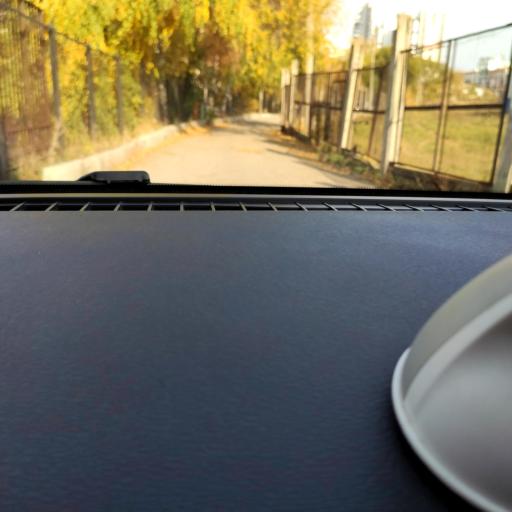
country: RU
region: Samara
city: Samara
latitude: 53.2358
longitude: 50.1842
